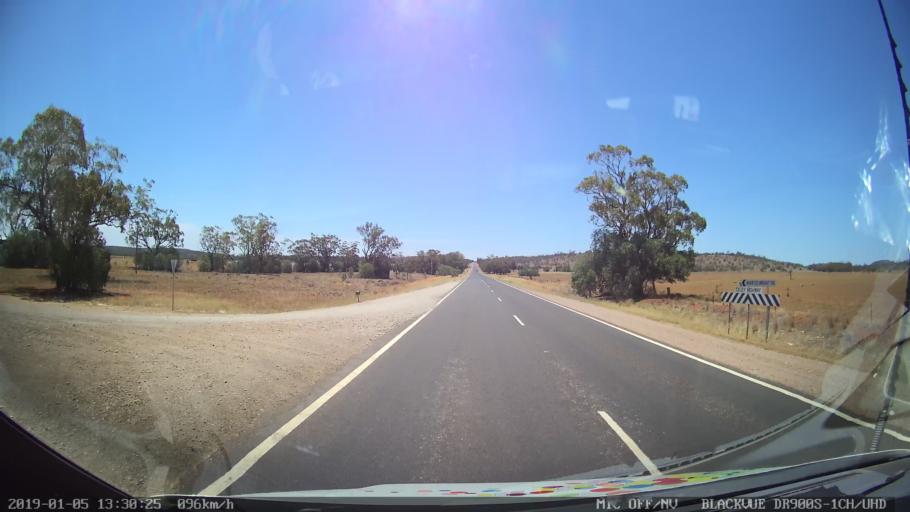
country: AU
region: New South Wales
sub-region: Gunnedah
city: Gunnedah
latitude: -31.0191
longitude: 150.0704
